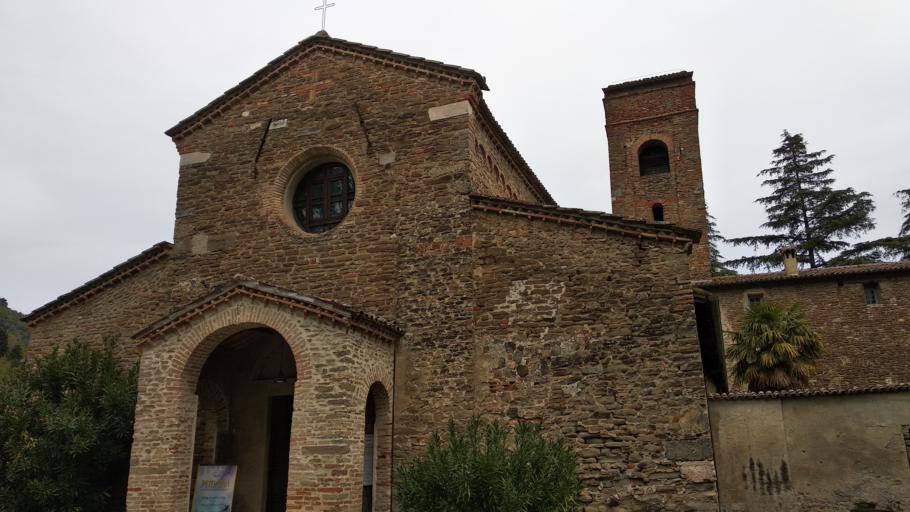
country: IT
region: Emilia-Romagna
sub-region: Provincia di Ravenna
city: Fognano
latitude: 44.2143
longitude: 11.7528
